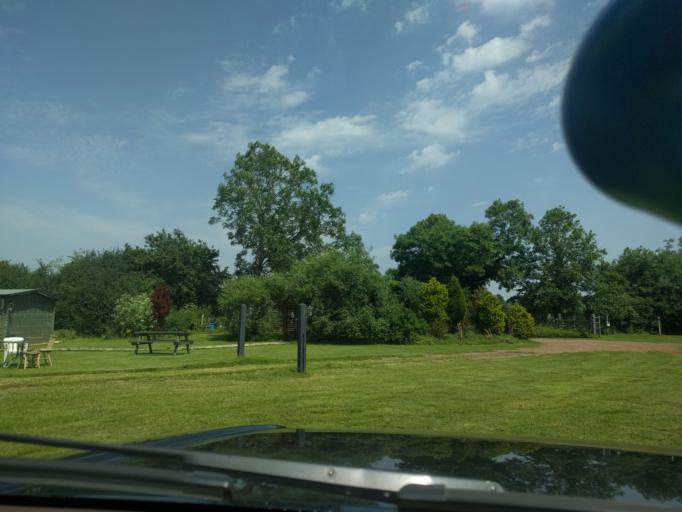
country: GB
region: England
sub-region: Wiltshire
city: Bradford-on-Avon
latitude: 51.3781
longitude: -2.2535
